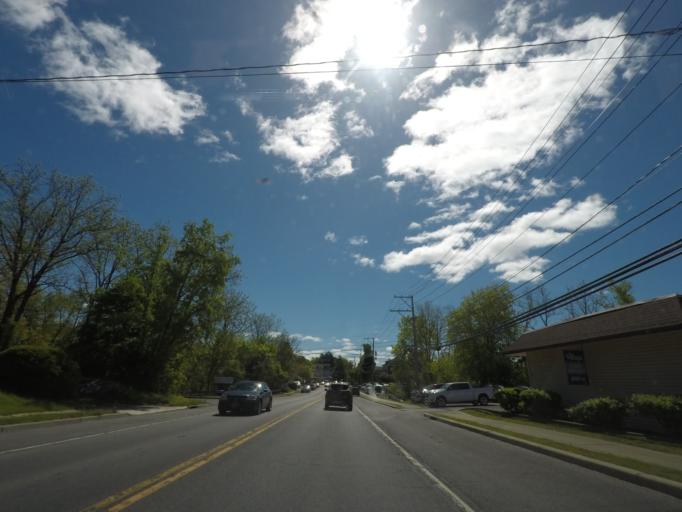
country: US
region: New York
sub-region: Ulster County
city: Saugerties
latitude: 42.0815
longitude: -73.9627
